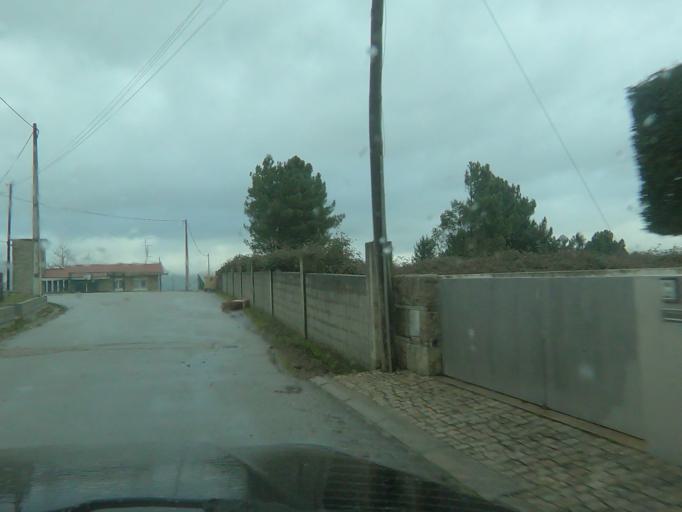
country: PT
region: Vila Real
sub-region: Vila Real
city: Vila Real
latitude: 41.2757
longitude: -7.7270
